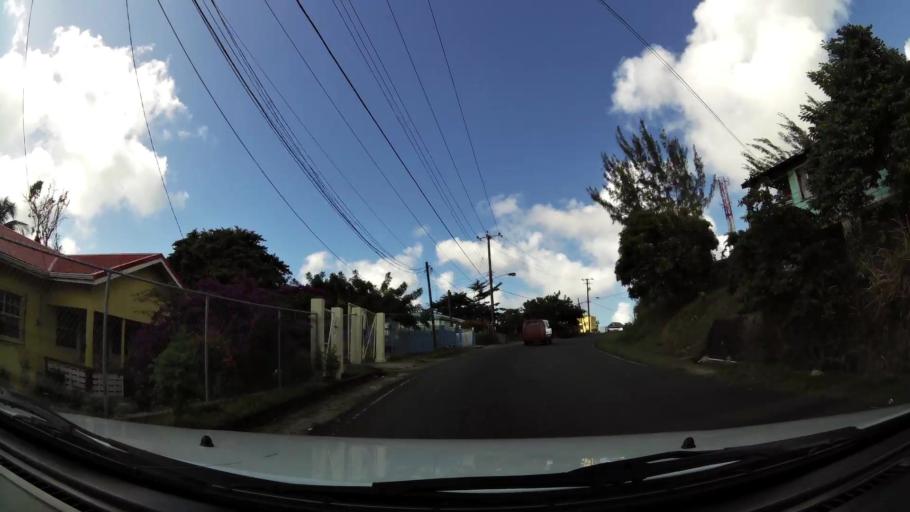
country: LC
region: Castries Quarter
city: Castries
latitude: 13.9983
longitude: -61.0008
